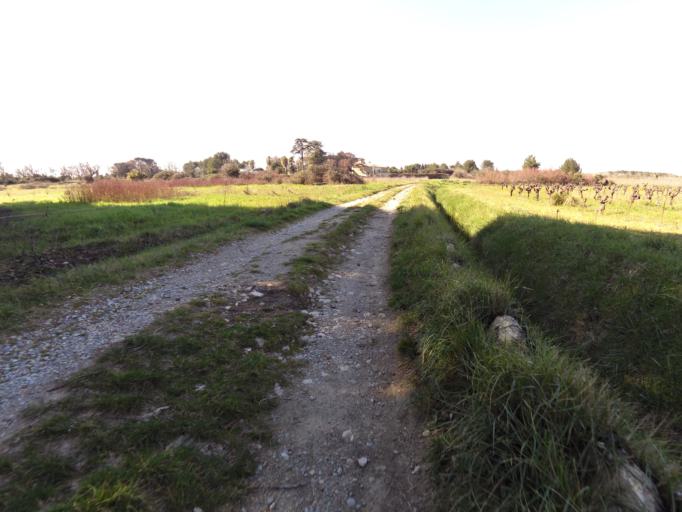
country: FR
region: Languedoc-Roussillon
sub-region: Departement du Gard
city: Aigues-Vives
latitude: 43.7436
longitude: 4.1757
